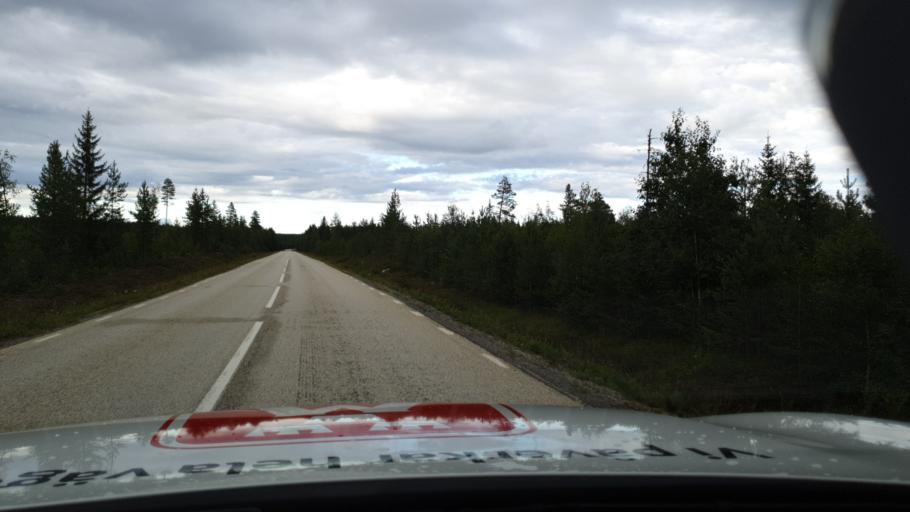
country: SE
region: Jaemtland
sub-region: Bergs Kommun
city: Hoverberg
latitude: 62.6922
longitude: 14.2277
